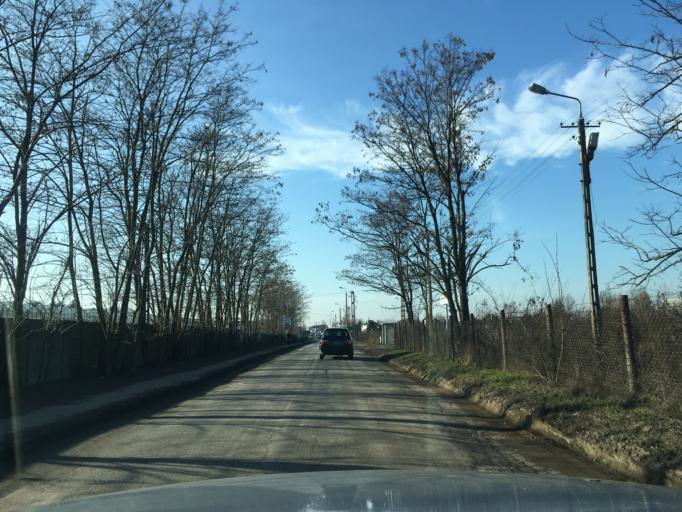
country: PL
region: Masovian Voivodeship
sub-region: Powiat piaseczynski
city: Lesznowola
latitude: 52.0574
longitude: 20.8731
